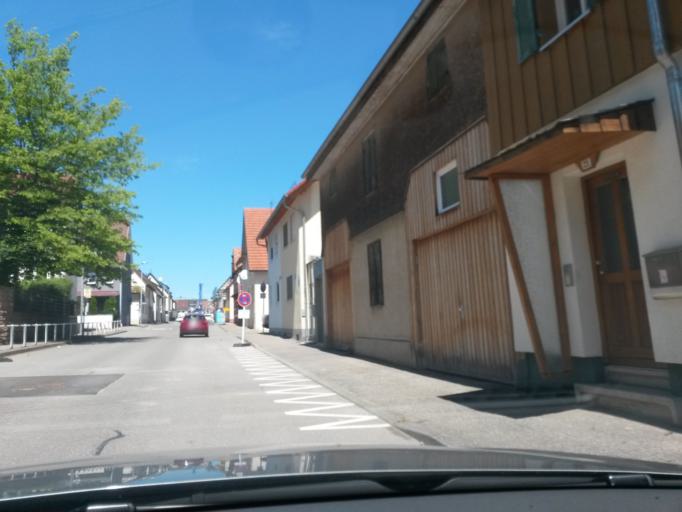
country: DE
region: Baden-Wuerttemberg
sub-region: Regierungsbezirk Stuttgart
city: Weil der Stadt
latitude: 48.7673
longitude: 8.8507
